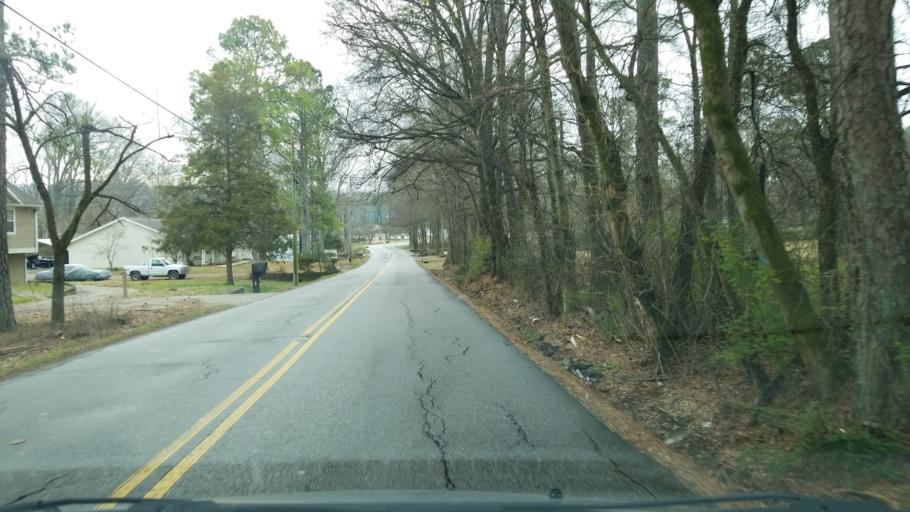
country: US
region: Tennessee
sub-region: Hamilton County
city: East Brainerd
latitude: 34.9873
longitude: -85.1479
